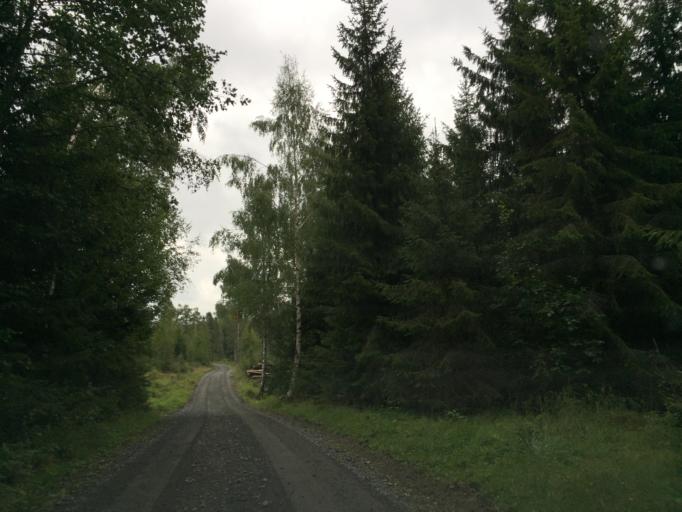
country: NO
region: Akershus
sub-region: Baerum
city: Sandvika
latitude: 60.0164
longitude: 10.5552
